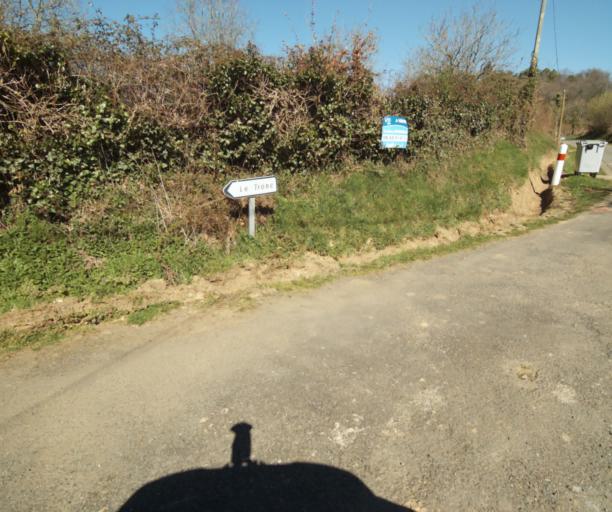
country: FR
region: Limousin
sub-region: Departement de la Correze
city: Saint-Clement
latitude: 45.3543
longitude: 1.6615
